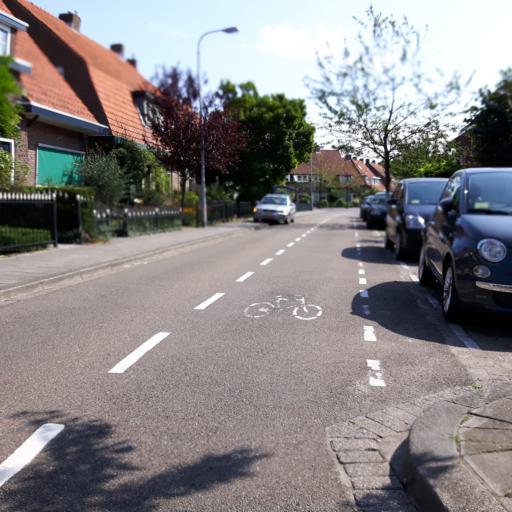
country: NL
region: Zeeland
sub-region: Gemeente Goes
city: Goes
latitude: 51.5020
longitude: 3.8958
